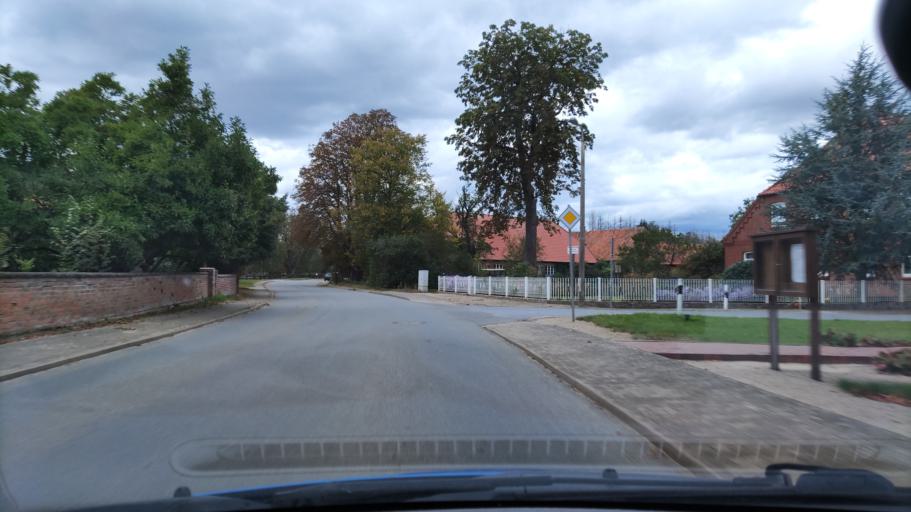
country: DE
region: Lower Saxony
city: Neu Darchau
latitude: 53.3187
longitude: 10.9551
